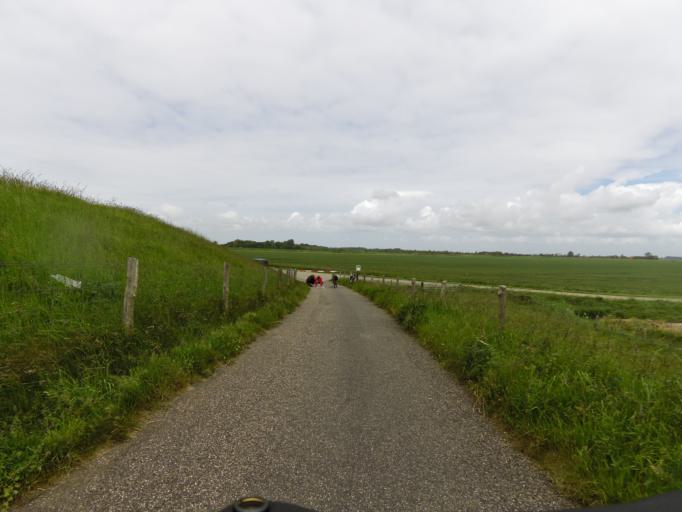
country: NL
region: Zeeland
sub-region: Schouwen-Duiveland
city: Bruinisse
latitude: 51.6302
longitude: 4.0537
